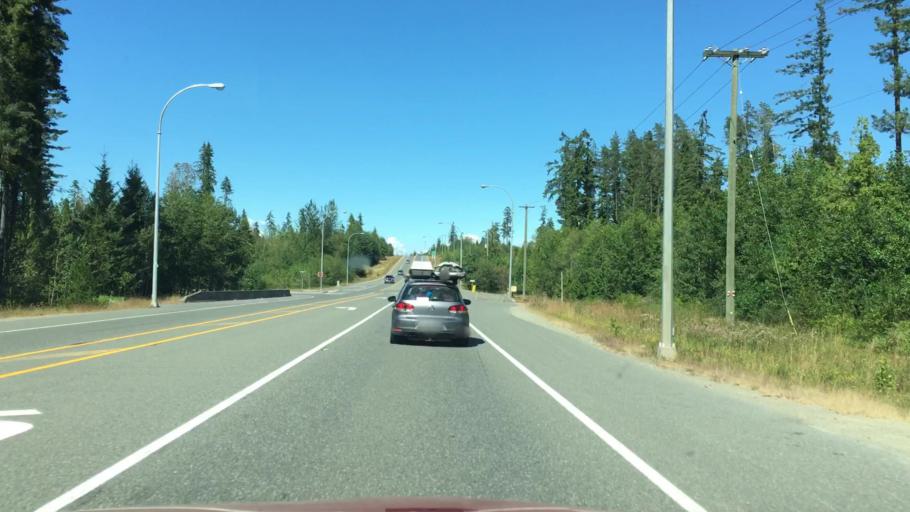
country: CA
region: British Columbia
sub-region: Regional District of Nanaimo
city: Parksville
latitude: 49.3147
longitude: -124.4471
